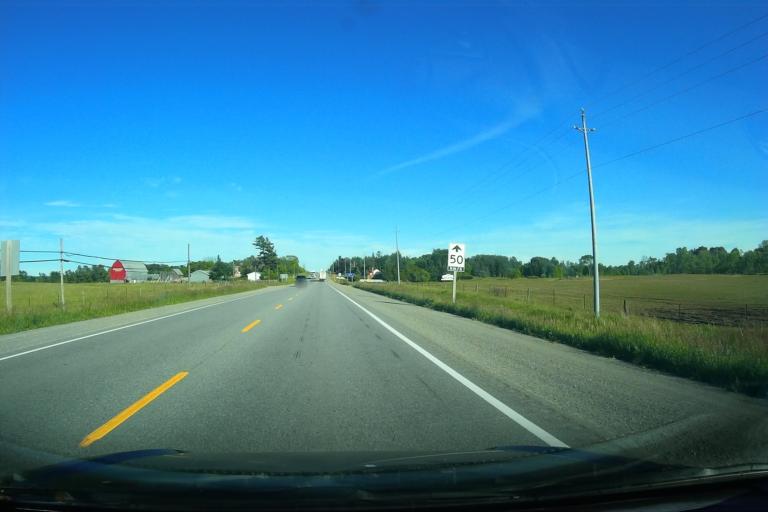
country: CA
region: Quebec
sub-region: Outaouais
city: Fort-Coulonge
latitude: 45.6364
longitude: -76.8922
